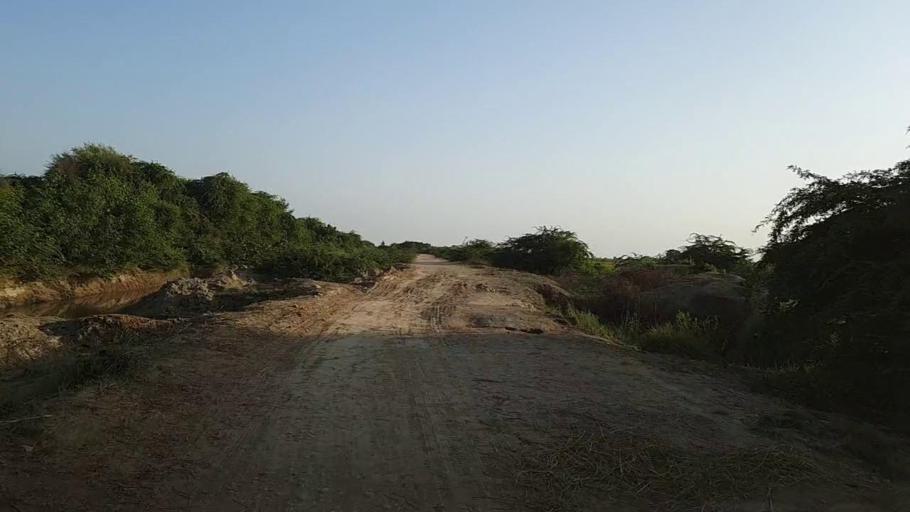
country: PK
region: Sindh
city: Kario
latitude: 24.7103
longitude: 68.6667
